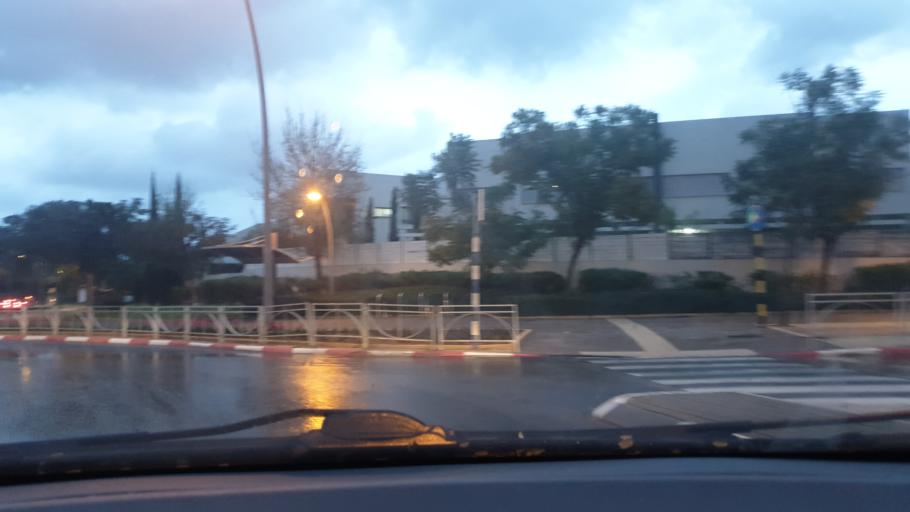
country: IL
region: Central District
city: Rishon LeZiyyon
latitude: 31.9825
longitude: 34.8025
